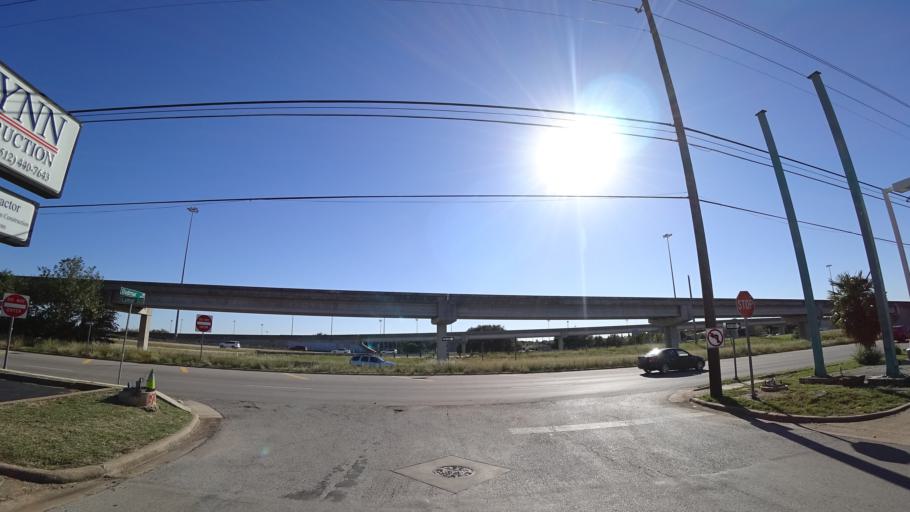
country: US
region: Texas
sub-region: Travis County
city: Rollingwood
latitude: 30.2334
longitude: -97.8084
